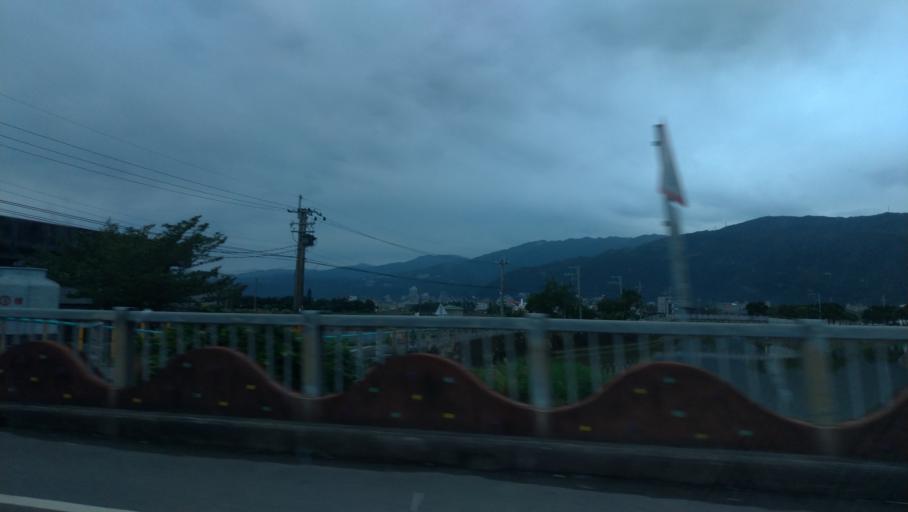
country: TW
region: Taiwan
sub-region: Yilan
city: Yilan
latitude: 24.8293
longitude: 121.8018
